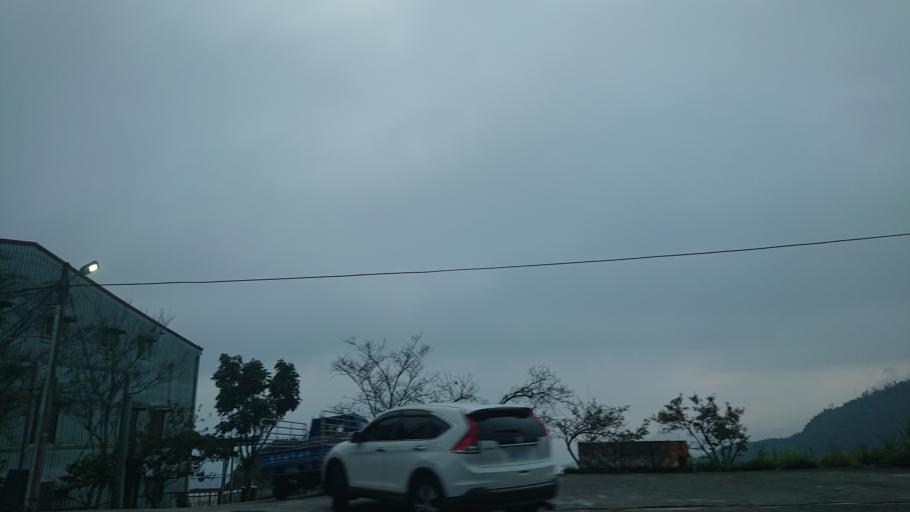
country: TW
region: Taiwan
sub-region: Chiayi
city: Jiayi Shi
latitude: 23.4723
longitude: 120.7031
